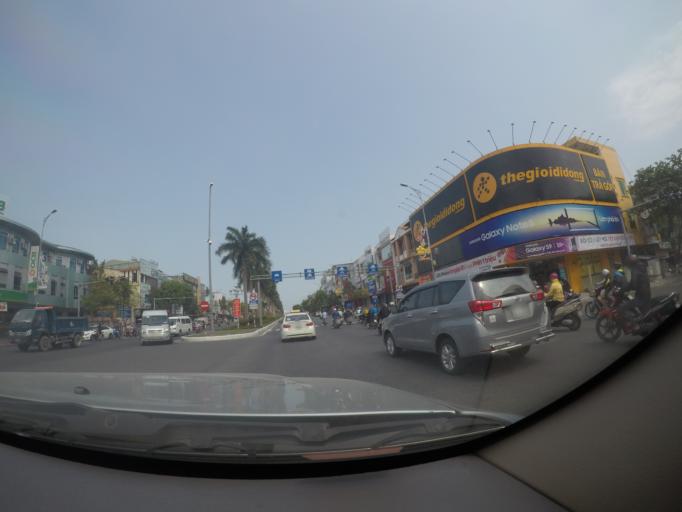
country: VN
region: Da Nang
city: Thanh Khe
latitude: 16.0659
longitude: 108.1920
